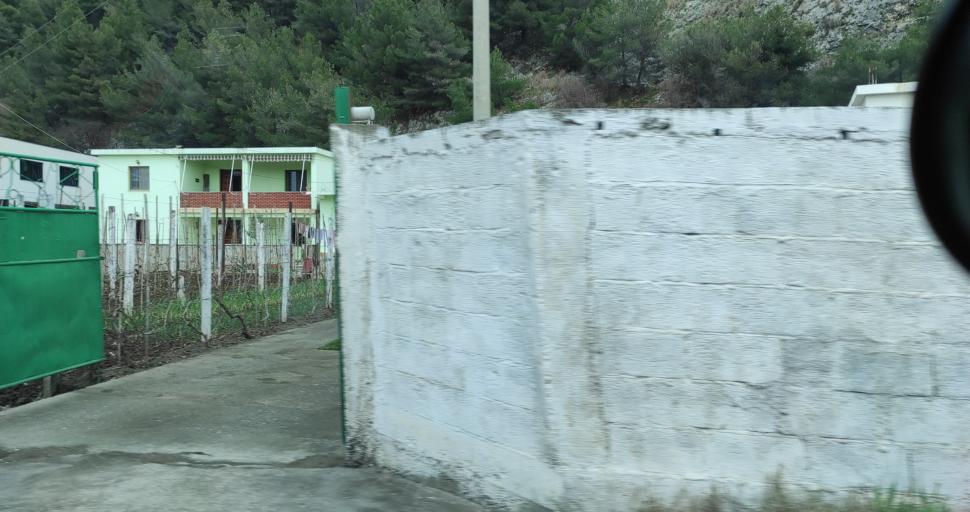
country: AL
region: Lezhe
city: Lezhe
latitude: 41.7911
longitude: 19.6238
